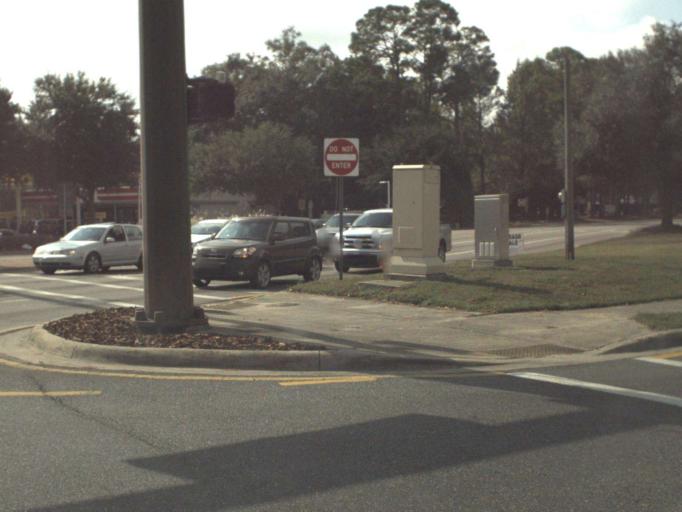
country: US
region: Florida
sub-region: Leon County
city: Tallahassee
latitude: 30.4784
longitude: -84.2368
